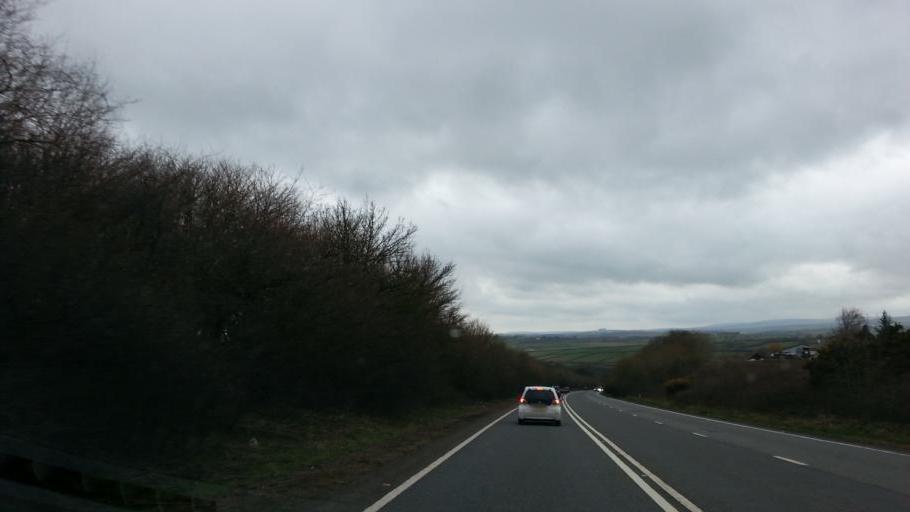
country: GB
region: England
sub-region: Devon
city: South Molton
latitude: 50.9862
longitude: -3.7025
